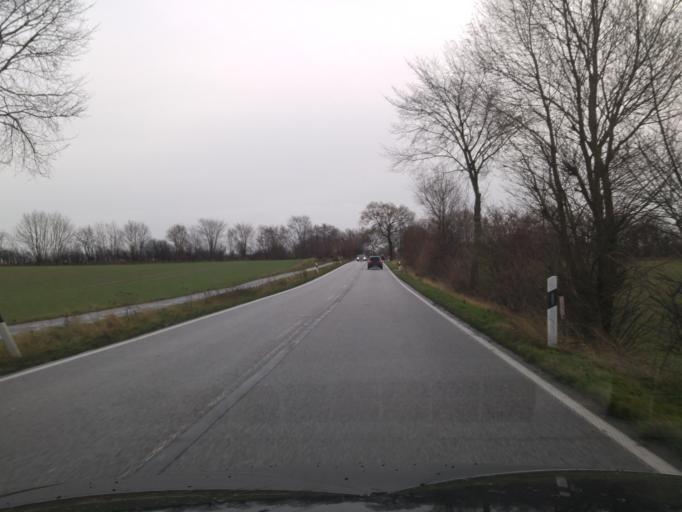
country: DE
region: Schleswig-Holstein
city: Travemuende
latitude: 53.9805
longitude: 10.8470
